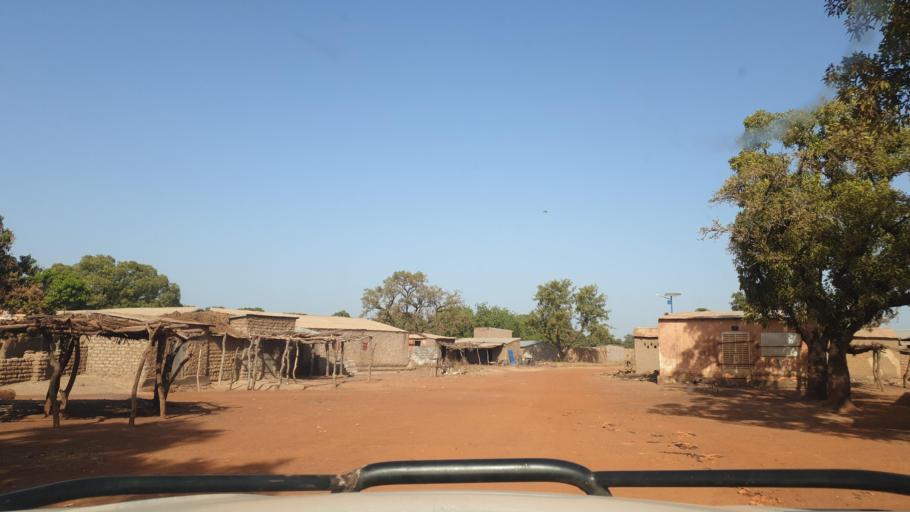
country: ML
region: Sikasso
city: Kolondieba
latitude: 11.7297
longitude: -6.8887
